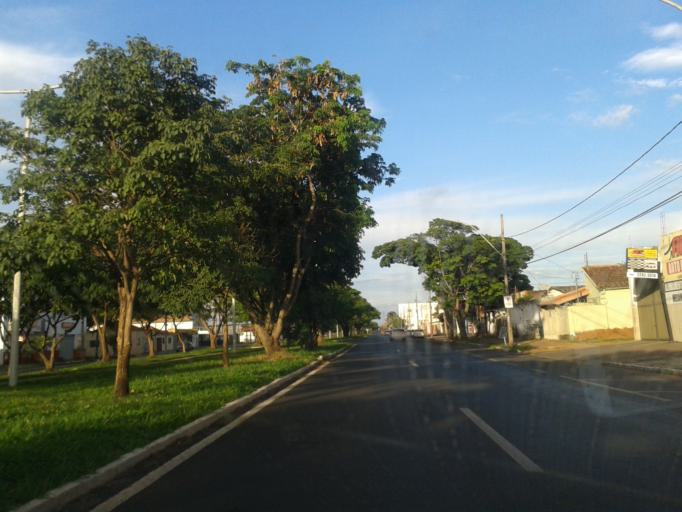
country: BR
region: Minas Gerais
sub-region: Araguari
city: Araguari
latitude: -18.6406
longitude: -48.1884
